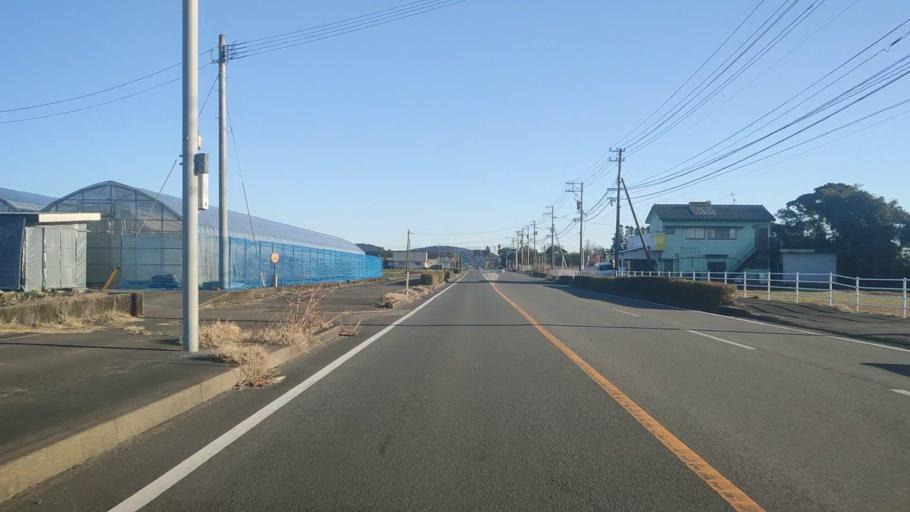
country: JP
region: Miyazaki
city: Takanabe
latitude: 32.3203
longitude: 131.5943
